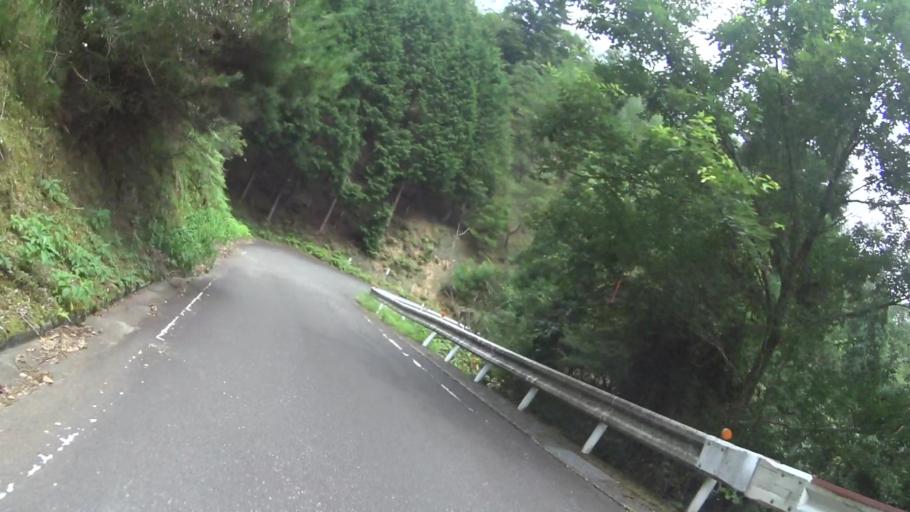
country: JP
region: Kyoto
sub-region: Kyoto-shi
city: Kamigyo-ku
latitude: 35.2051
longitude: 135.6720
